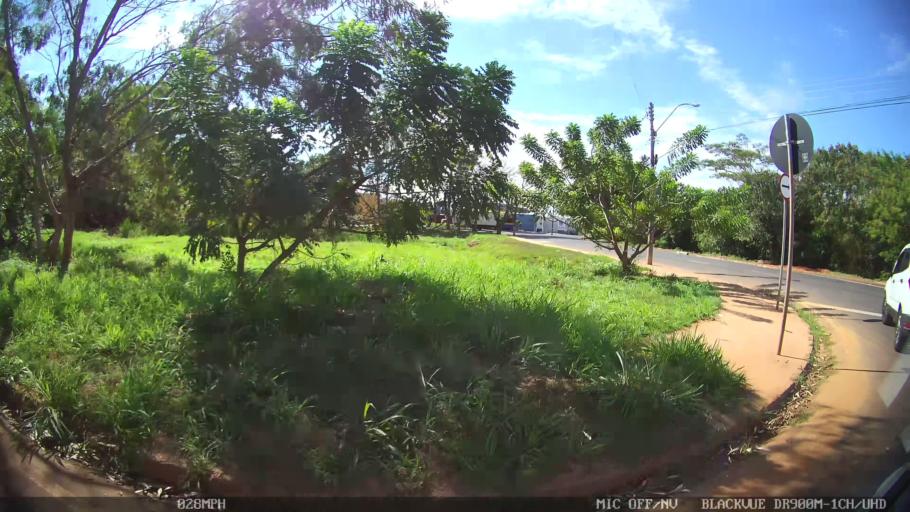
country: BR
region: Sao Paulo
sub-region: Sao Jose Do Rio Preto
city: Sao Jose do Rio Preto
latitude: -20.8447
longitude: -49.3592
